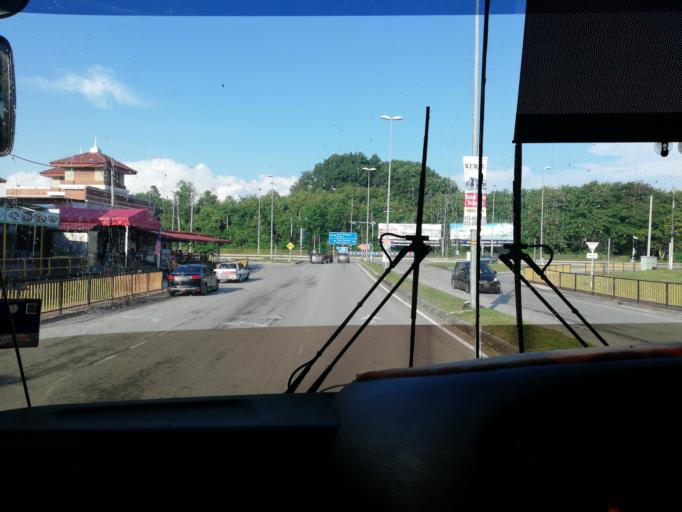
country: MY
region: Negeri Sembilan
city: Port Dickson
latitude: 2.4412
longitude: 101.8619
